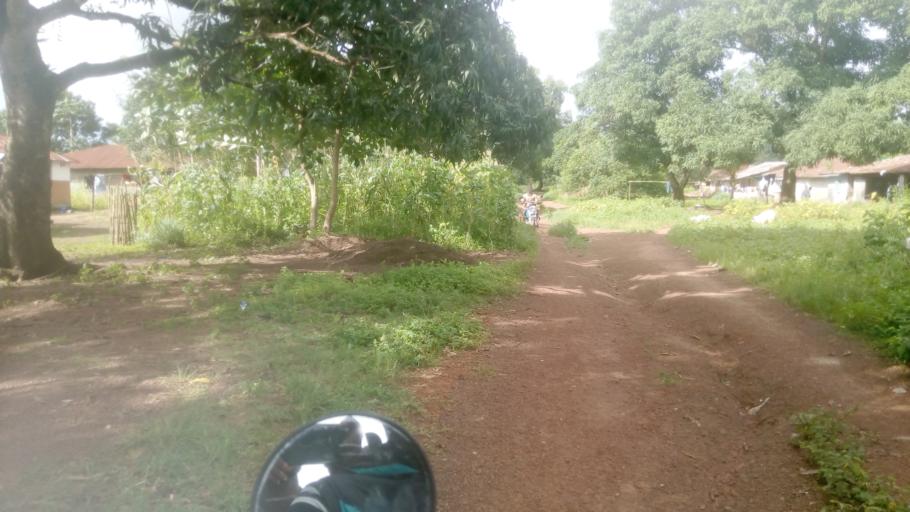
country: SL
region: Northern Province
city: Port Loko
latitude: 8.7096
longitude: -12.6796
